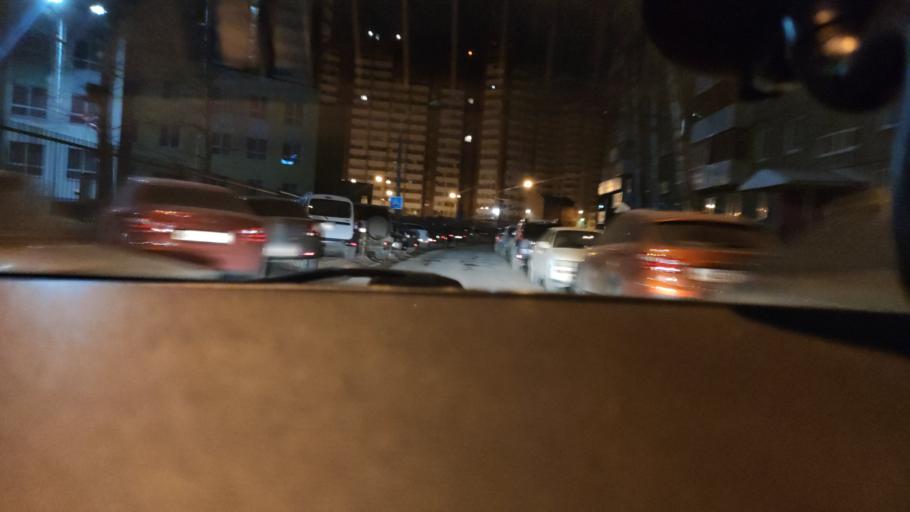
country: RU
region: Perm
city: Perm
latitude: 57.9845
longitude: 56.2869
